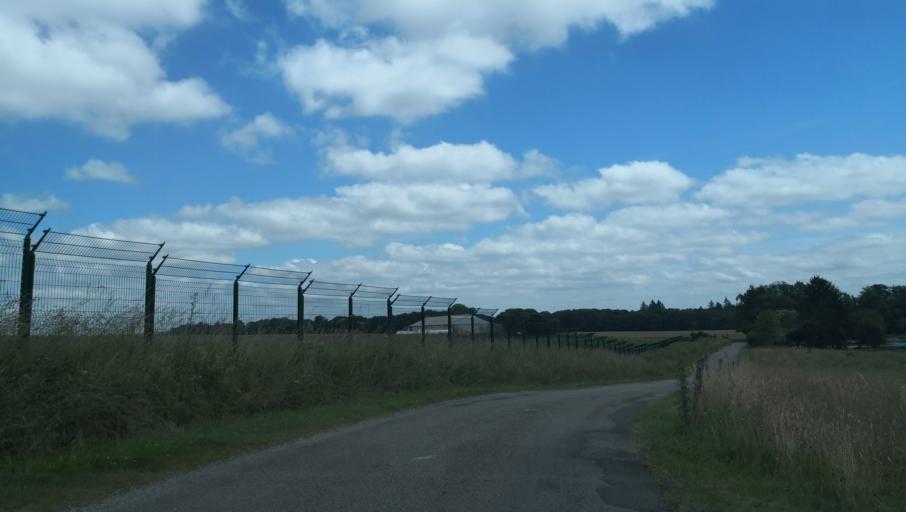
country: FR
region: Limousin
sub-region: Departement de la Haute-Vienne
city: Isle
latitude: 45.8520
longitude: 1.1743
